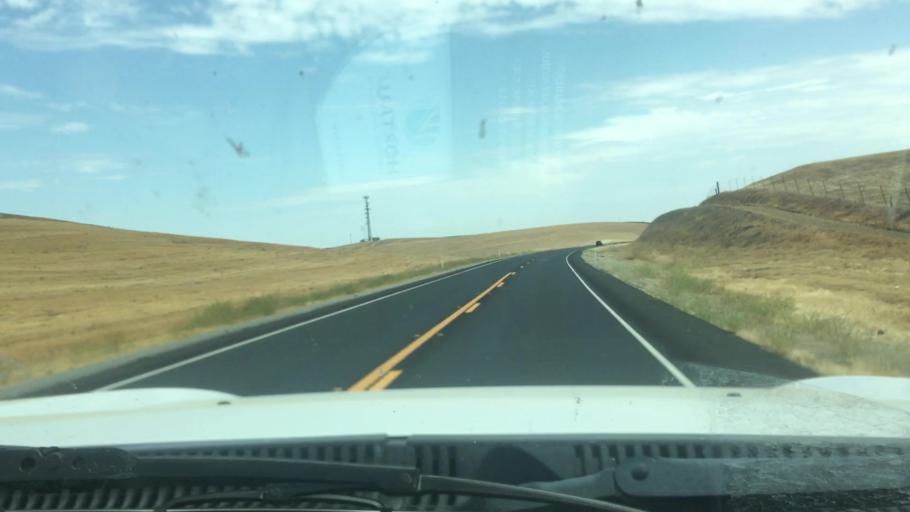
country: US
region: California
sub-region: Tulare County
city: Richgrove
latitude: 35.6507
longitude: -119.0800
